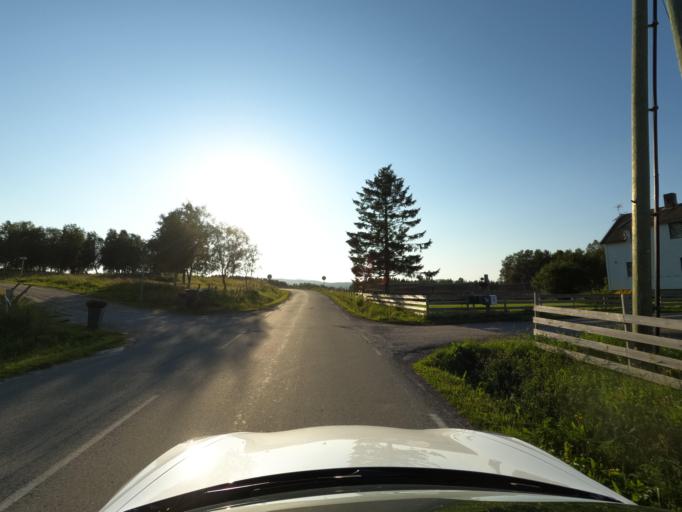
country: NO
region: Troms
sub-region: Skanland
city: Evenskjer
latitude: 68.4592
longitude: 16.6937
